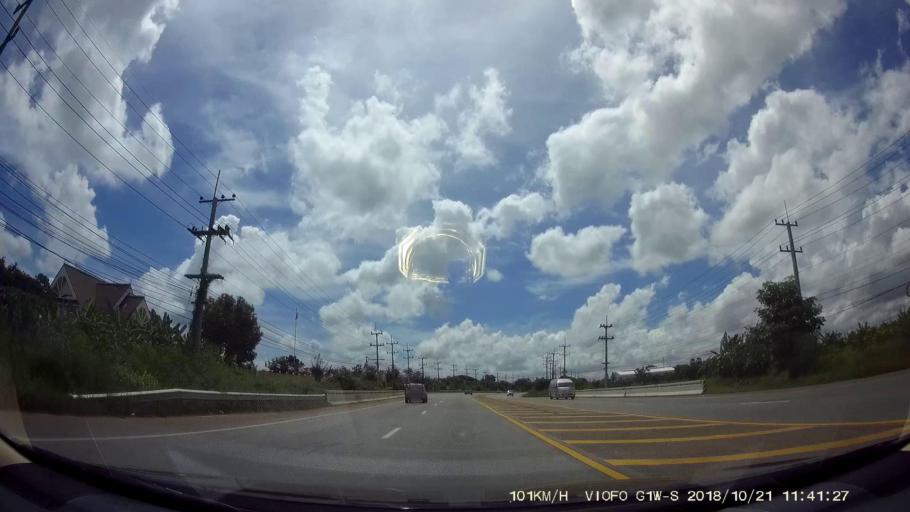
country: TH
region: Chaiyaphum
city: Chaiyaphum
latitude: 15.6986
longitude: 102.0145
